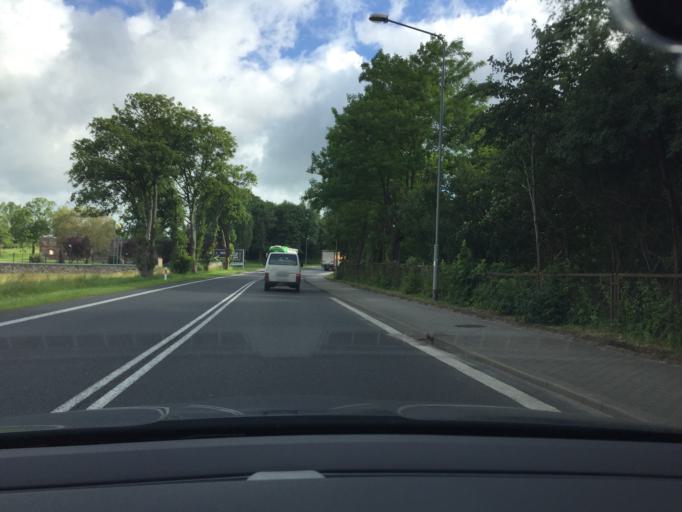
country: PL
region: West Pomeranian Voivodeship
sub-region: Powiat kolobrzeski
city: Ryman
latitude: 53.9404
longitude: 15.5248
